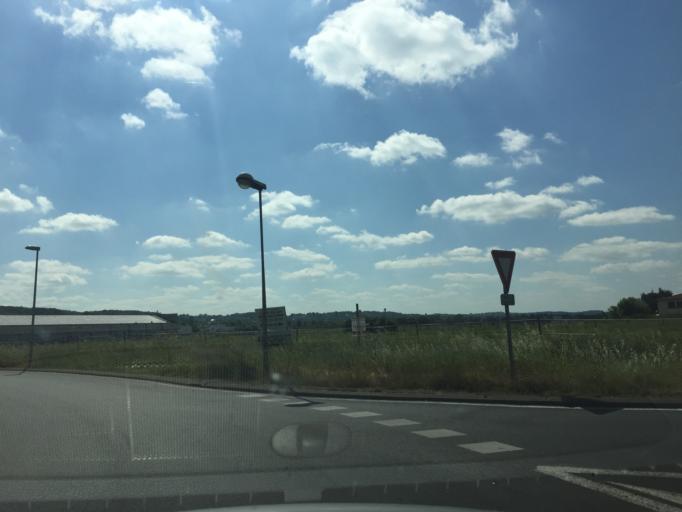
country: FR
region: Aquitaine
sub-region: Departement du Lot-et-Garonne
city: Boe
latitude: 44.1699
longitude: 0.6087
